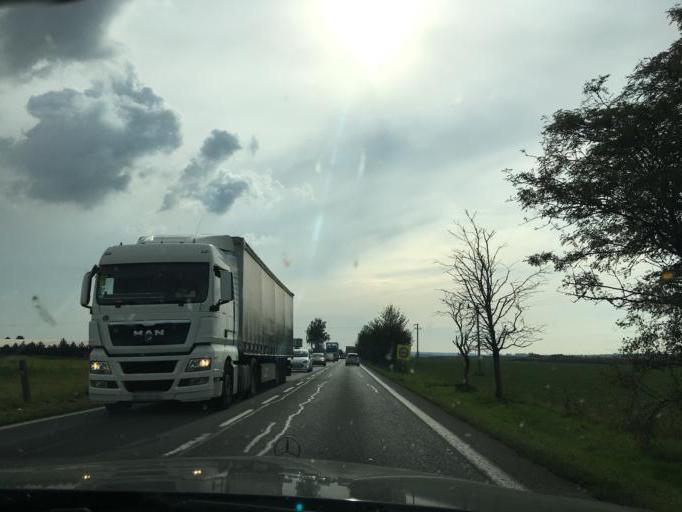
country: CZ
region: Kralovehradecky
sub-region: Okres Hradec Kralove
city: Smirice
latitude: 50.3033
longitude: 15.8518
